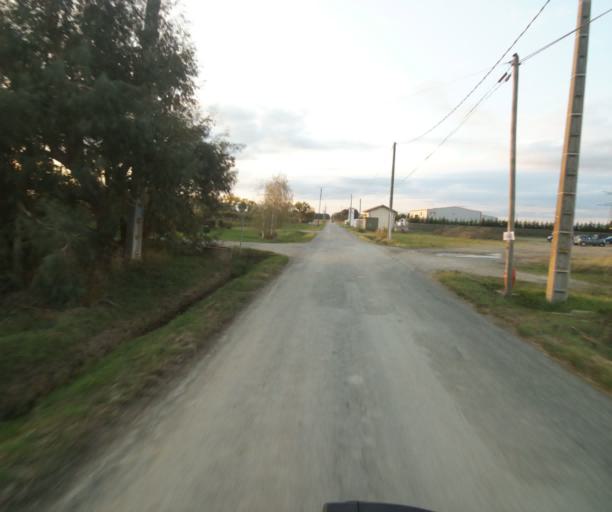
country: FR
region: Midi-Pyrenees
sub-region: Departement du Tarn-et-Garonne
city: Verdun-sur-Garonne
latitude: 43.8218
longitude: 1.2420
